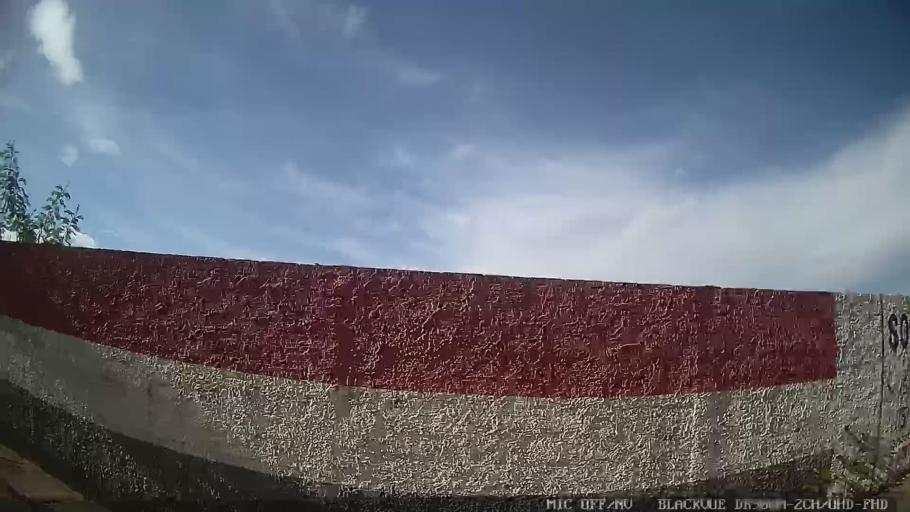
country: BR
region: Sao Paulo
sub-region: Tiete
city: Tiete
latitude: -23.0942
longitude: -47.7056
